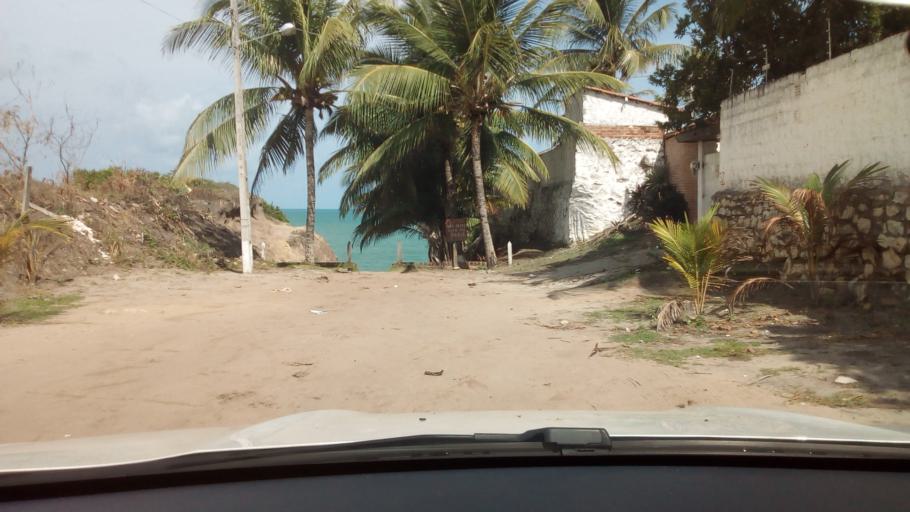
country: BR
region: Paraiba
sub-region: Conde
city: Conde
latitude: -7.2959
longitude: -34.8020
